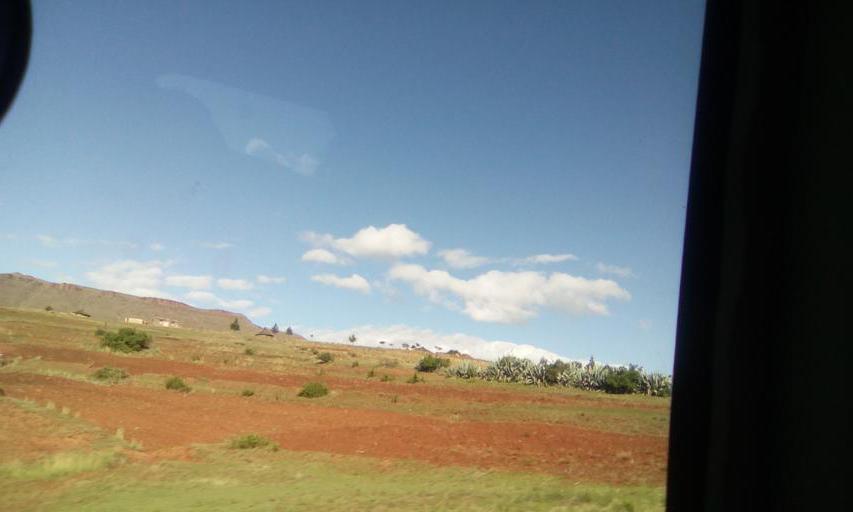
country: LS
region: Qacha's Nek
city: Qacha's Nek
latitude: -30.0565
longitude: 28.2981
